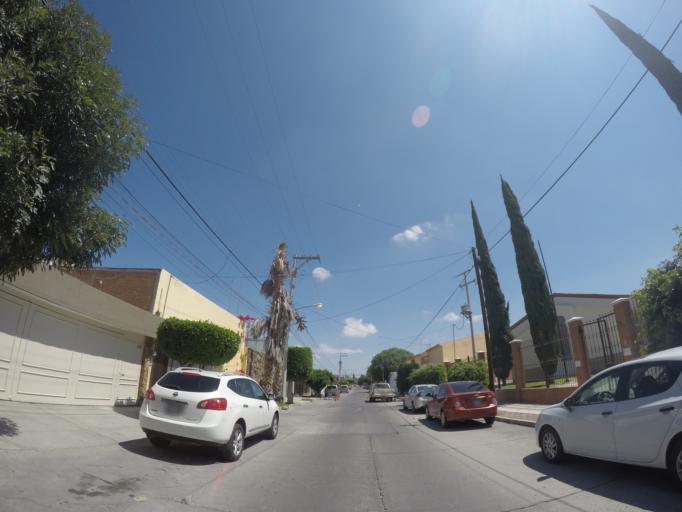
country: MX
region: San Luis Potosi
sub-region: San Luis Potosi
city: San Luis Potosi
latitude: 22.1421
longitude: -101.0087
